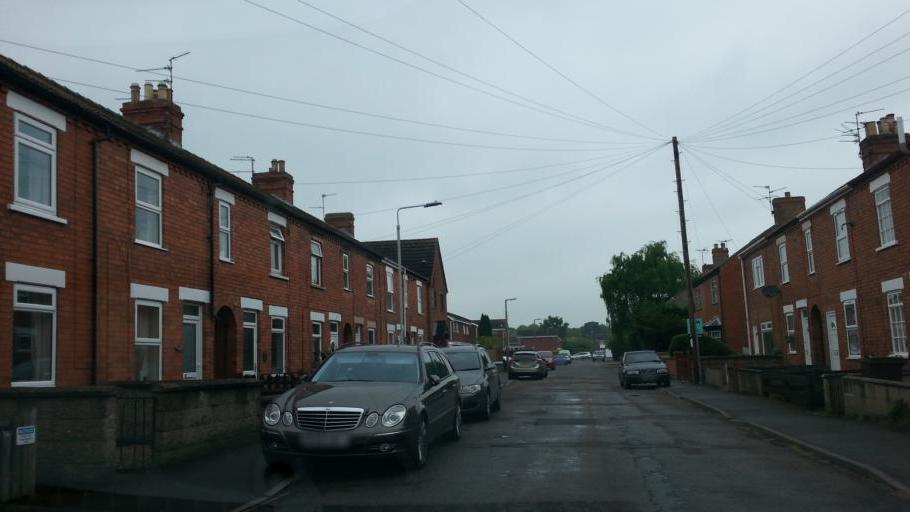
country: GB
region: England
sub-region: Nottinghamshire
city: Newark on Trent
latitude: 53.0629
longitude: -0.7920
